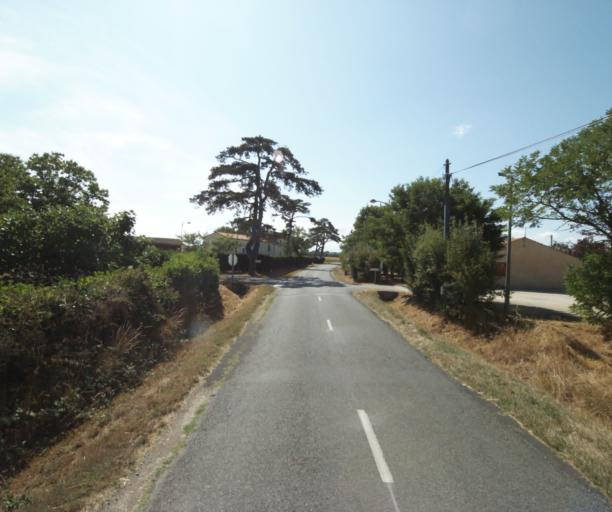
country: FR
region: Midi-Pyrenees
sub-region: Departement de la Haute-Garonne
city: Revel
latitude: 43.4900
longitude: 1.9824
